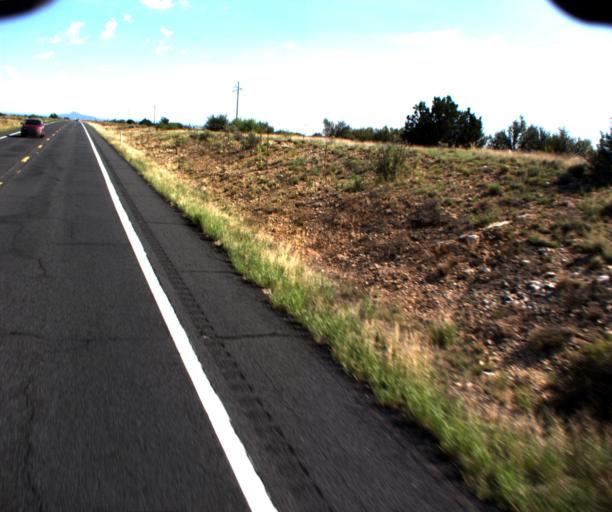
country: US
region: Arizona
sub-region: Coconino County
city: Williams
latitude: 35.5889
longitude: -112.1502
